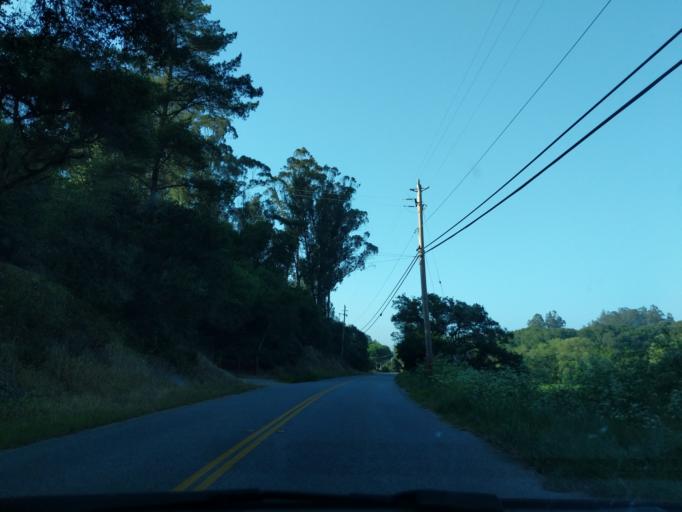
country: US
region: California
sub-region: Monterey County
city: Las Lomas
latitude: 36.8720
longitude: -121.6898
